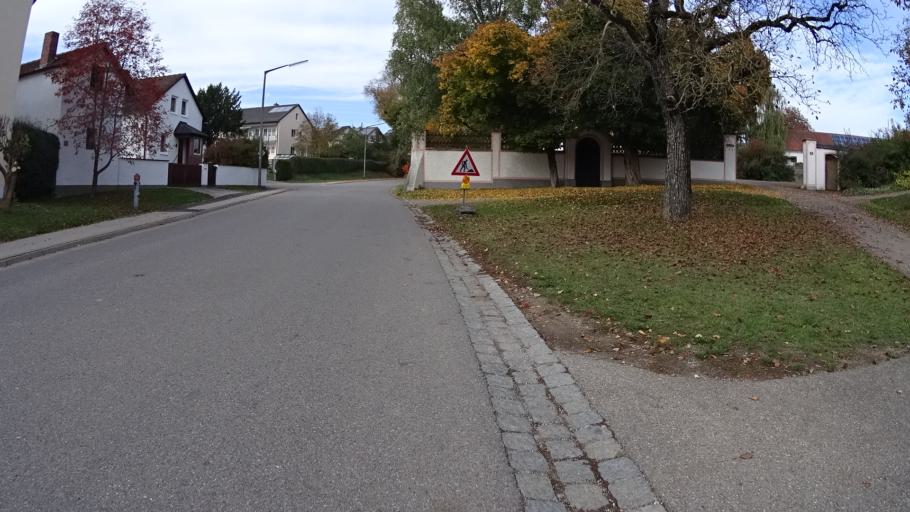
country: DE
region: Bavaria
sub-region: Upper Bavaria
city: Buxheim
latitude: 48.8260
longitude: 11.2755
